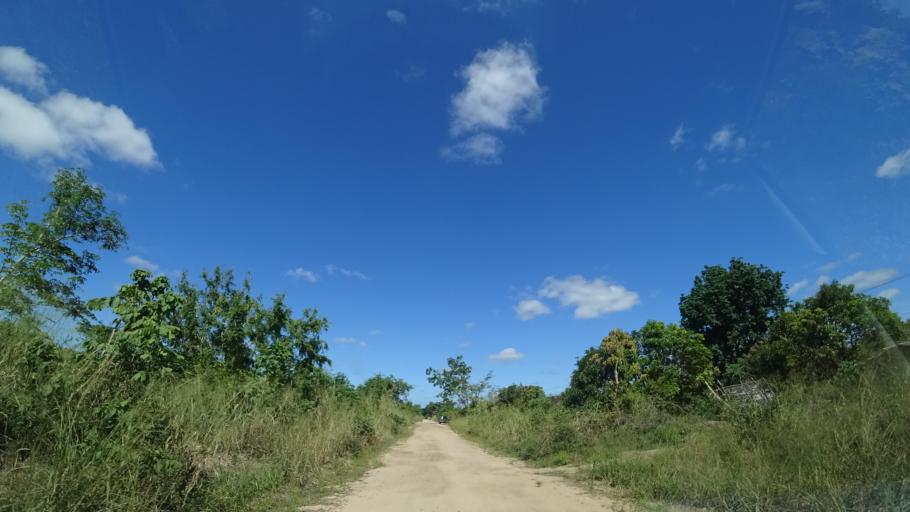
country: MZ
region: Sofala
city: Dondo
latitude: -19.3228
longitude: 34.6919
